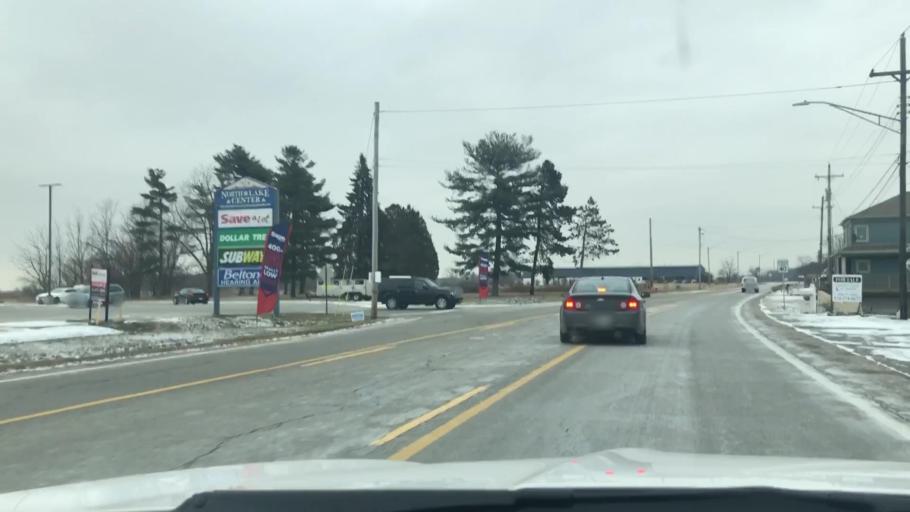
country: US
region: Indiana
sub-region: Fulton County
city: Rochester
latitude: 41.0622
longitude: -86.1827
